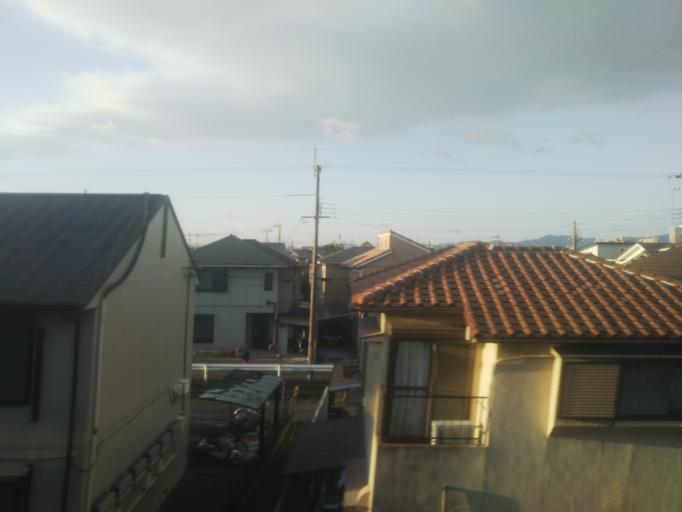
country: JP
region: Shiga Prefecture
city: Kusatsu
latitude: 35.0279
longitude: 135.9815
